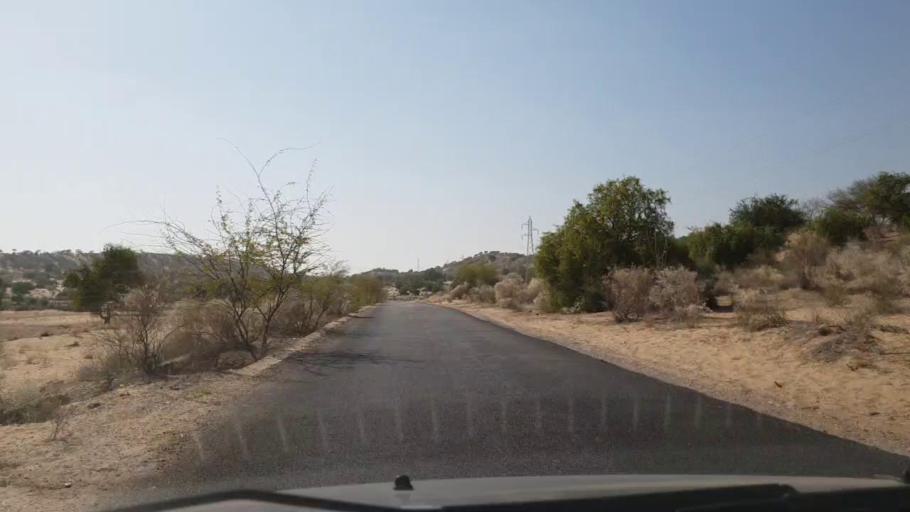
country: PK
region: Sindh
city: Mithi
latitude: 24.6818
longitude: 69.7798
